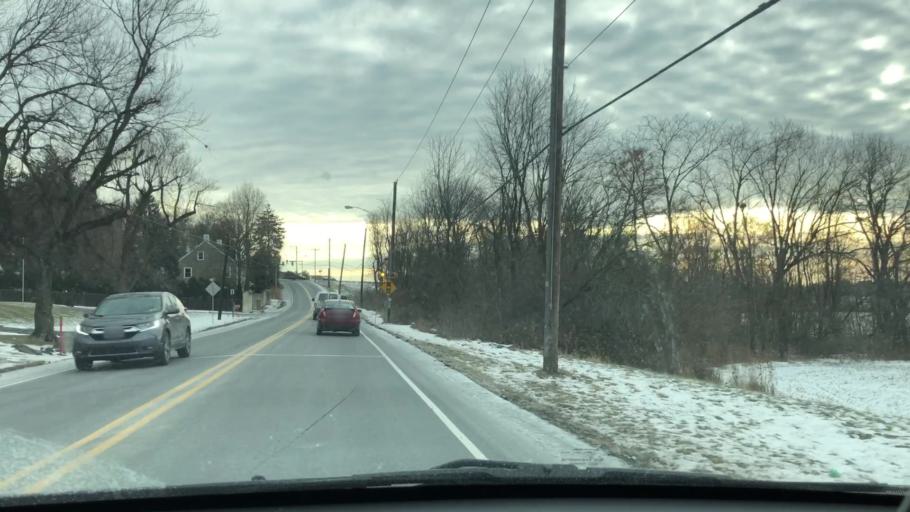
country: US
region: Pennsylvania
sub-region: Lancaster County
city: Landisville
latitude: 40.0553
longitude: -76.3838
